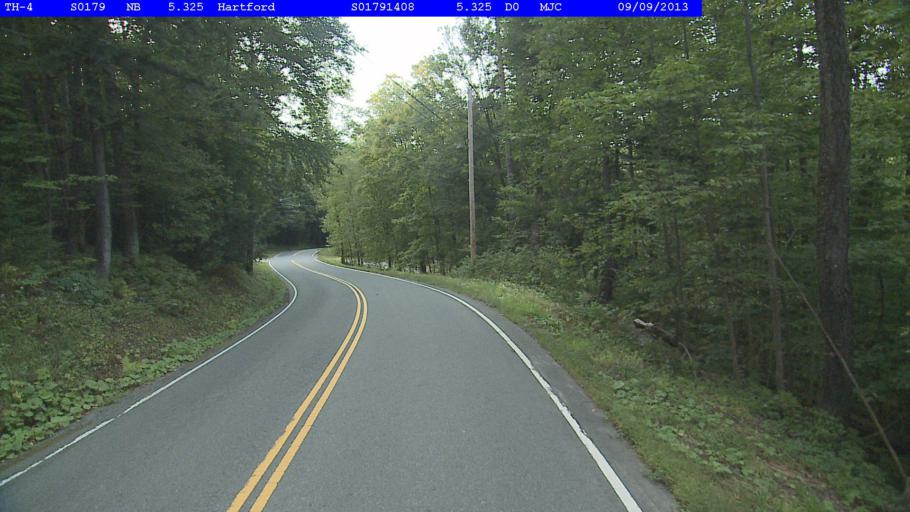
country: US
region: Vermont
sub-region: Windsor County
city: White River Junction
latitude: 43.7051
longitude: -72.4203
